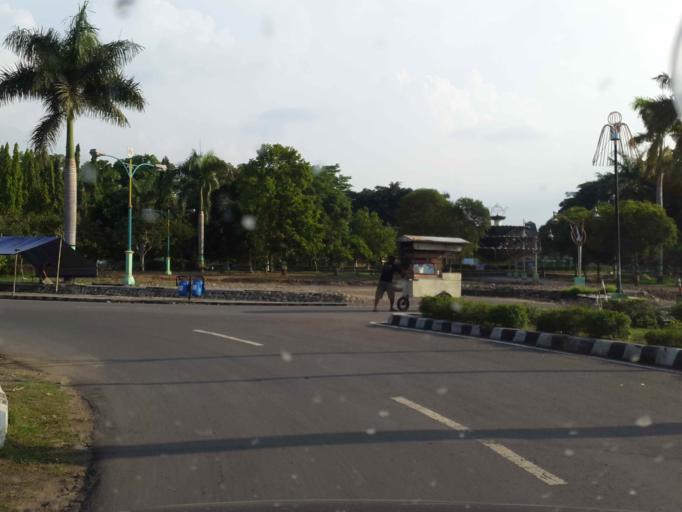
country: ID
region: Central Java
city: Slawi
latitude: -6.9920
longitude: 109.1278
